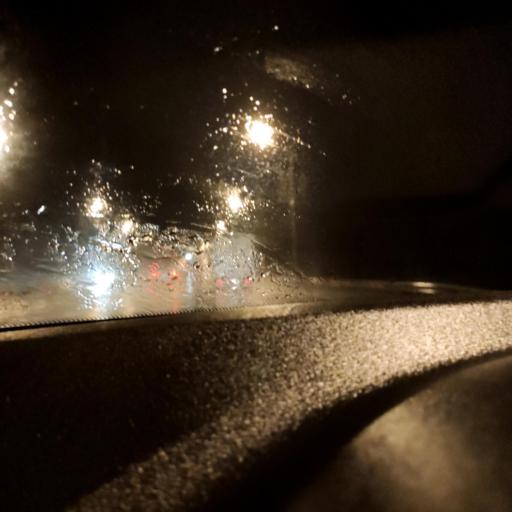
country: RU
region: Samara
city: Novosemeykino
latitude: 53.3350
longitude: 50.2320
